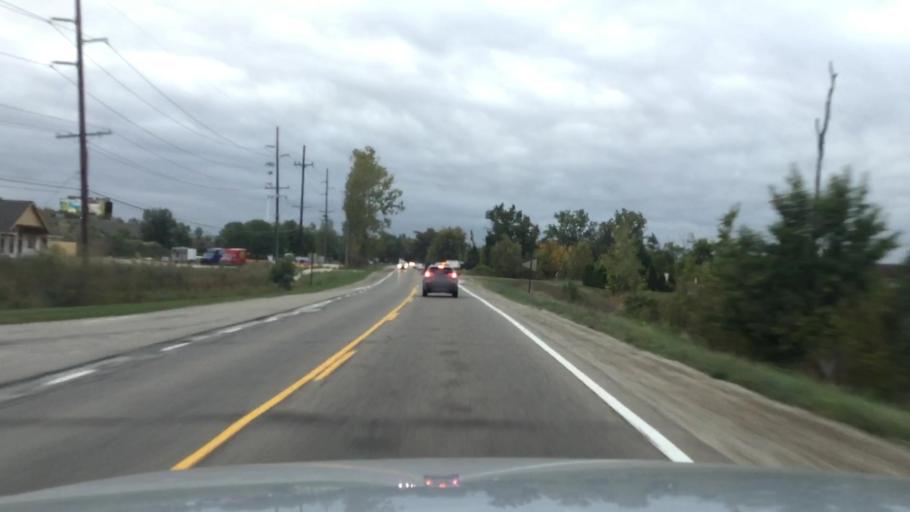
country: US
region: Michigan
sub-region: Livingston County
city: Brighton
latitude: 42.6210
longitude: -83.7513
